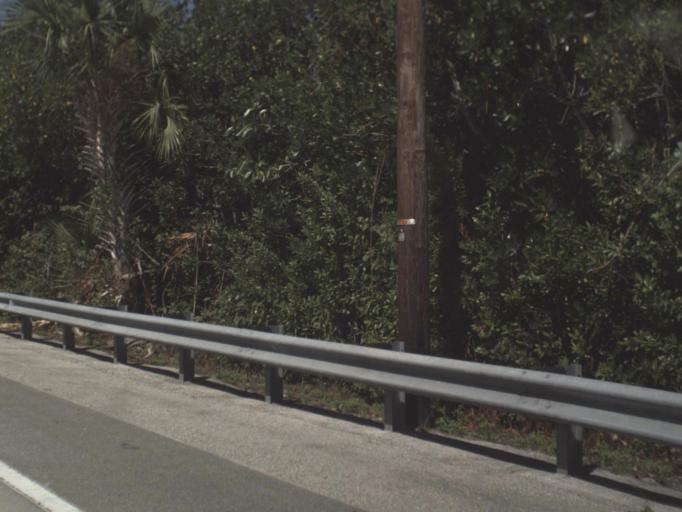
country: US
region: Florida
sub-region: Collier County
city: Marco
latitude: 25.9876
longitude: -81.5776
